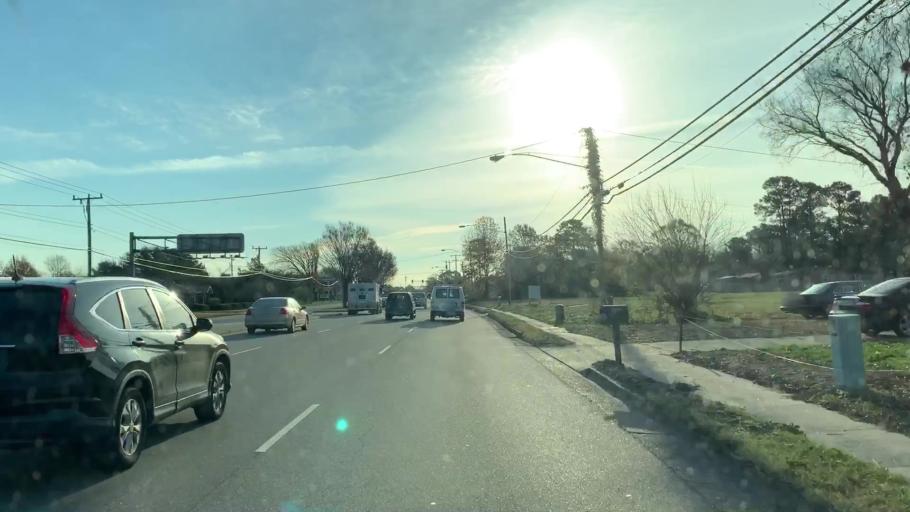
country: US
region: Virginia
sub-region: City of Chesapeake
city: Chesapeake
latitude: 36.8020
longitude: -76.1844
